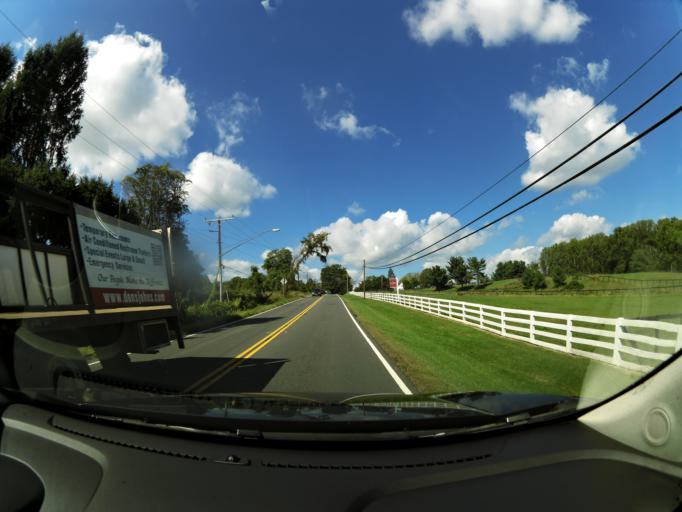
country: US
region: Virginia
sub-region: Fairfax County
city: Tysons Corner
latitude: 38.9639
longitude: -77.2310
